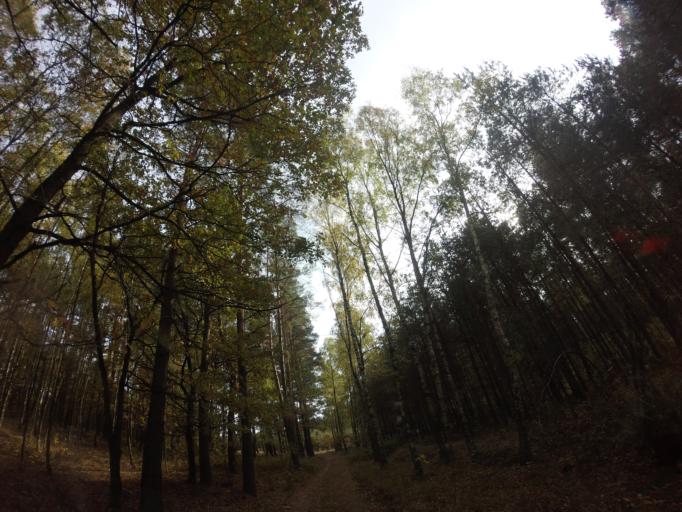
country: PL
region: West Pomeranian Voivodeship
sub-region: Powiat choszczenski
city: Drawno
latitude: 53.2540
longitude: 15.6741
